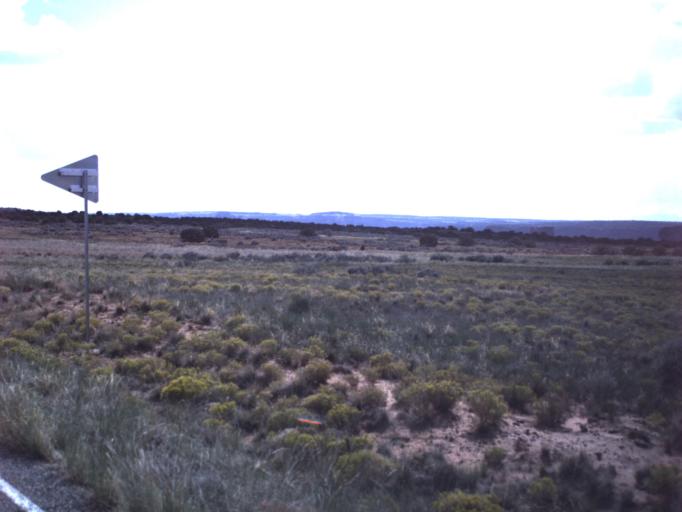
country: US
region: Utah
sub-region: Grand County
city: Moab
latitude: 38.5090
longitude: -109.7297
